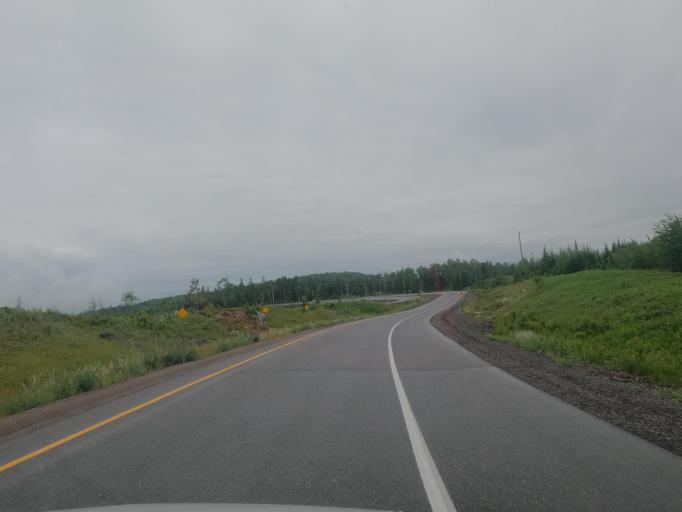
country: CA
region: Ontario
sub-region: Thunder Bay District
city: Thunder Bay
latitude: 48.4841
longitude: -89.1787
